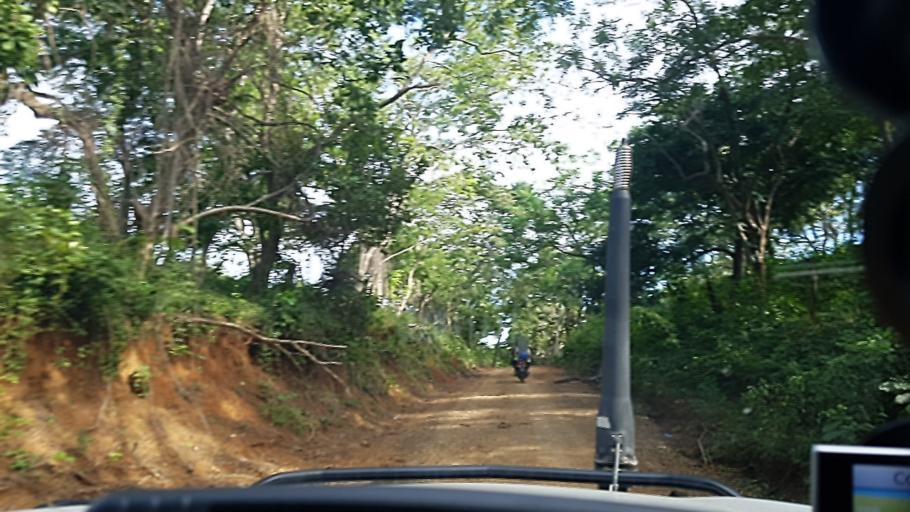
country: NI
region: Rivas
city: Tola
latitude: 11.5219
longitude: -86.1395
